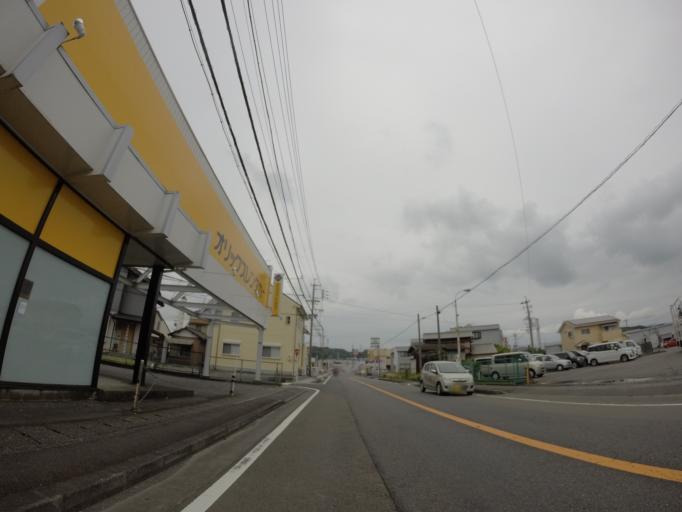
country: JP
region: Shizuoka
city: Fujieda
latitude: 34.8506
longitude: 138.2415
